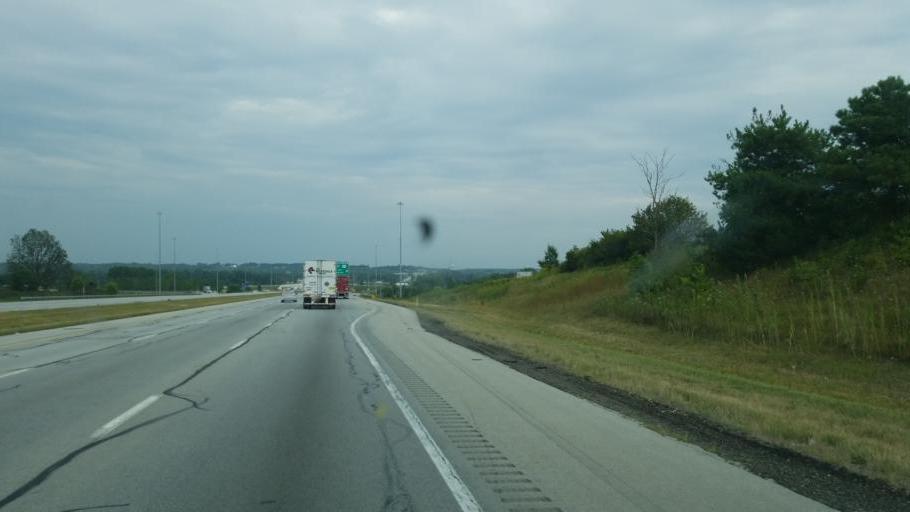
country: US
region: Ohio
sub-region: Medina County
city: Westfield Center
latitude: 41.0238
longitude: -81.9076
